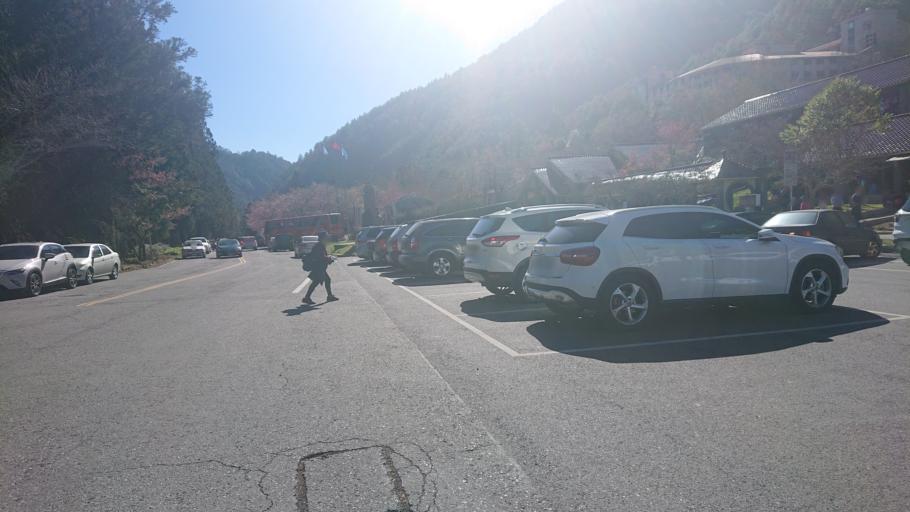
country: TW
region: Taiwan
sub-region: Hualien
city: Hualian
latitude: 24.3535
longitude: 121.3102
